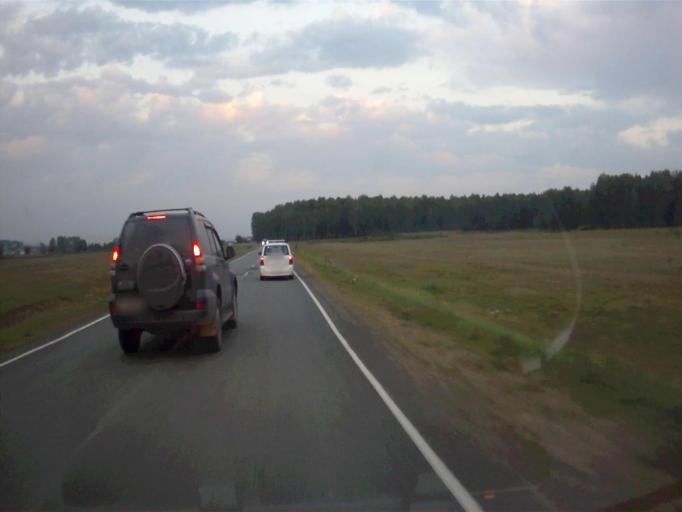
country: RU
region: Chelyabinsk
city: Chebarkul'
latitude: 55.1779
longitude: 60.4677
